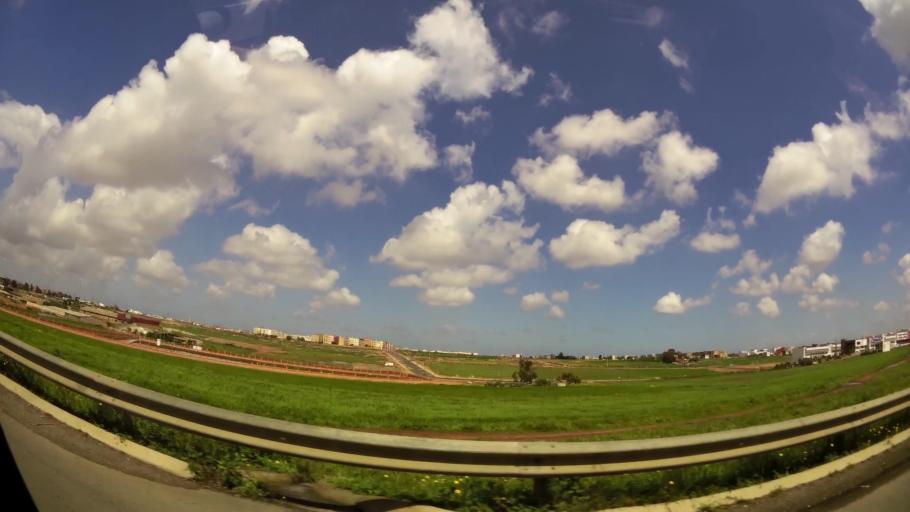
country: MA
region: Grand Casablanca
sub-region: Casablanca
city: Casablanca
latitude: 33.5303
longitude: -7.5623
